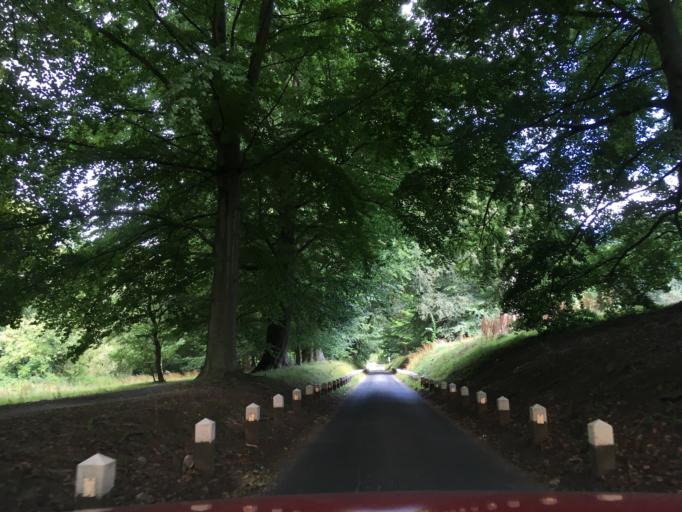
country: GB
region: England
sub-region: Kent
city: Maidstone
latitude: 51.2698
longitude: 0.5376
